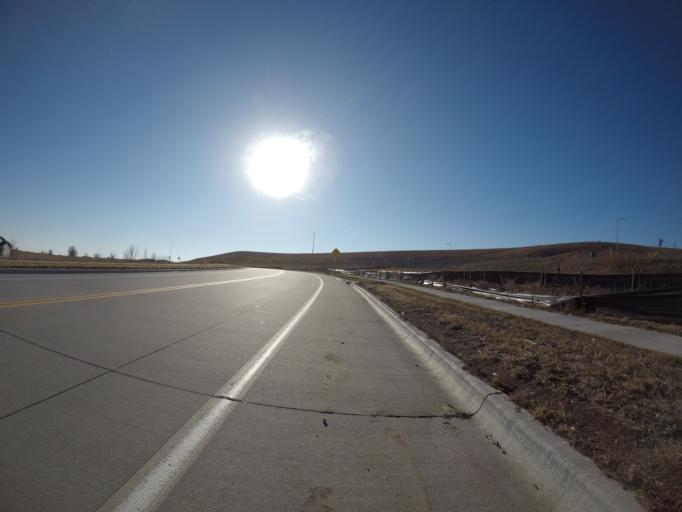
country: US
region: Kansas
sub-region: Riley County
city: Manhattan
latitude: 39.2166
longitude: -96.6453
